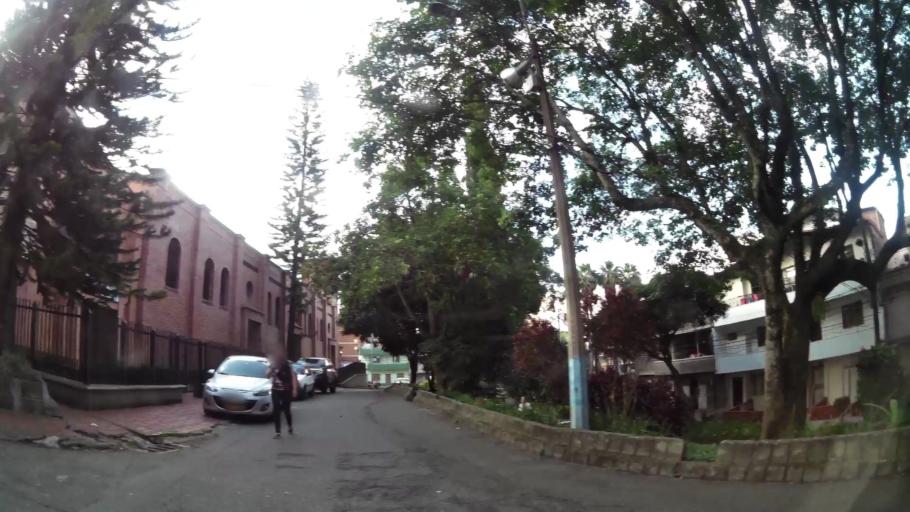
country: CO
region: Antioquia
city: Envigado
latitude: 6.1707
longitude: -75.5818
